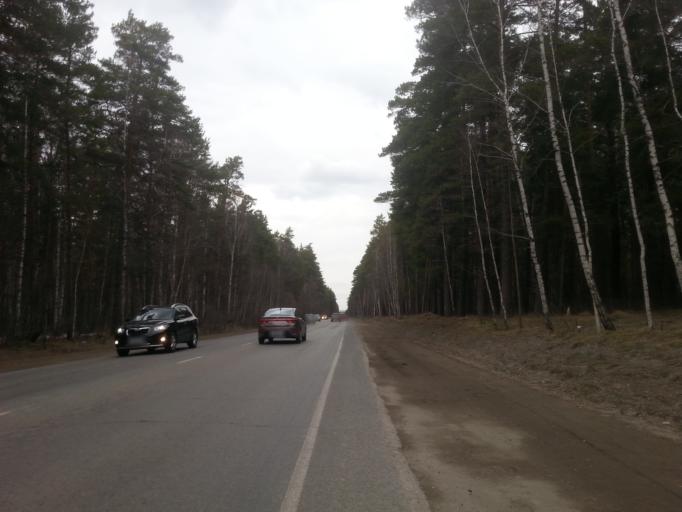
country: RU
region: Altai Krai
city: Yuzhnyy
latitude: 53.2781
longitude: 83.7188
